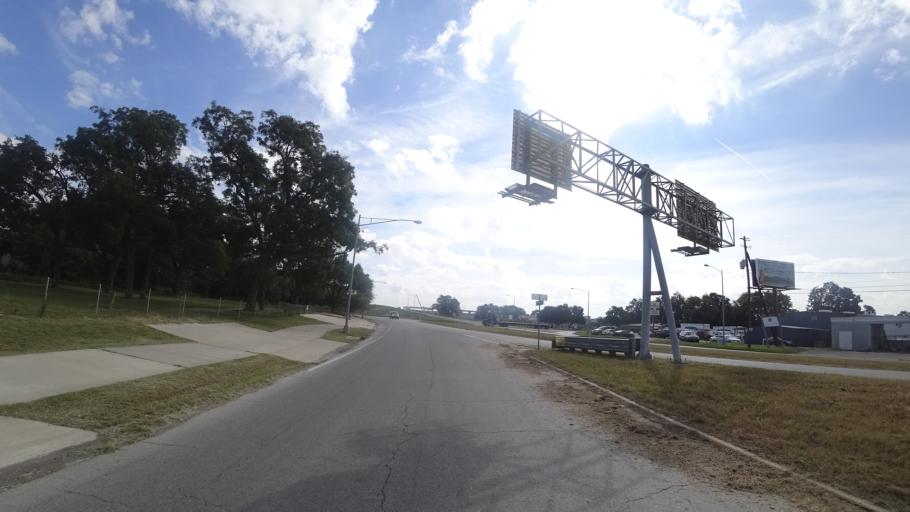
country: US
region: Texas
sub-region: Travis County
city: Austin
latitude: 30.2515
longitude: -97.6968
